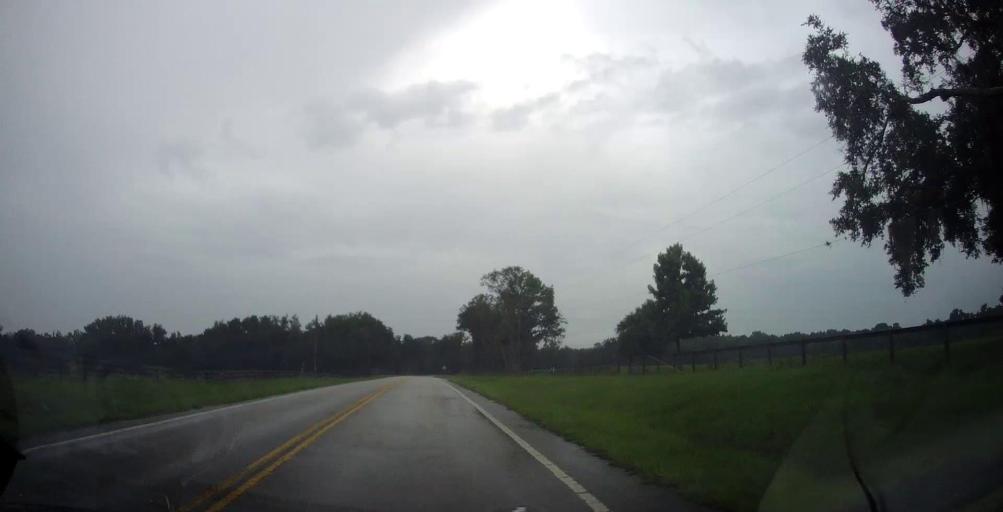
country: US
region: Florida
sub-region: Marion County
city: Citra
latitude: 29.4008
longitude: -82.2484
